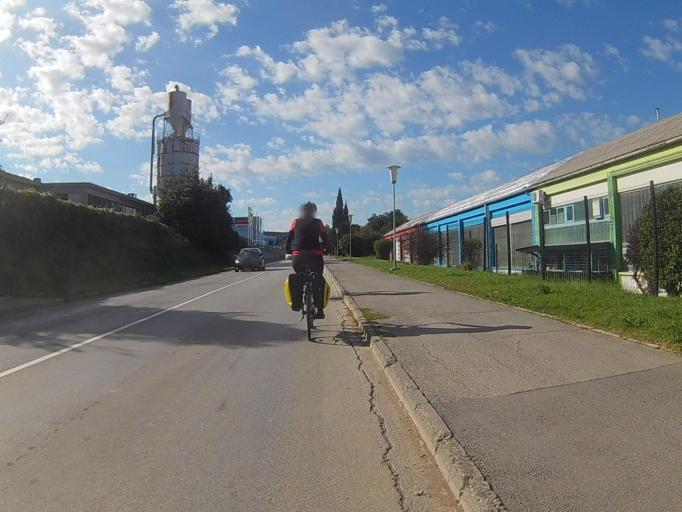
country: SI
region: Izola-Isola
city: Izola
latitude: 45.5358
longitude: 13.6709
